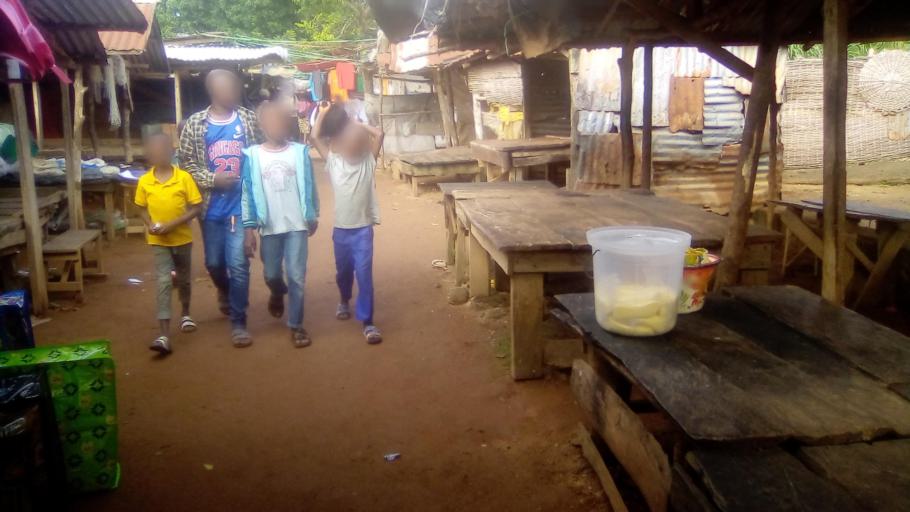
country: SL
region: Eastern Province
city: Kailahun
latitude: 8.2784
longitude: -10.5724
